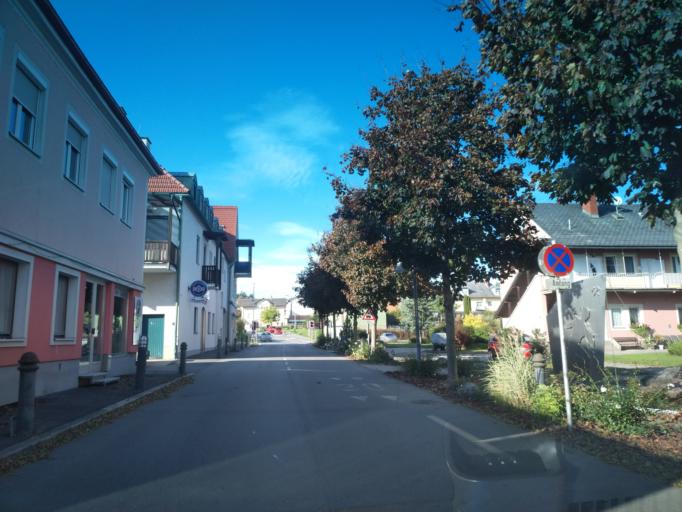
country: AT
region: Styria
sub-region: Politischer Bezirk Deutschlandsberg
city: Wies
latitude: 46.7285
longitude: 15.2969
